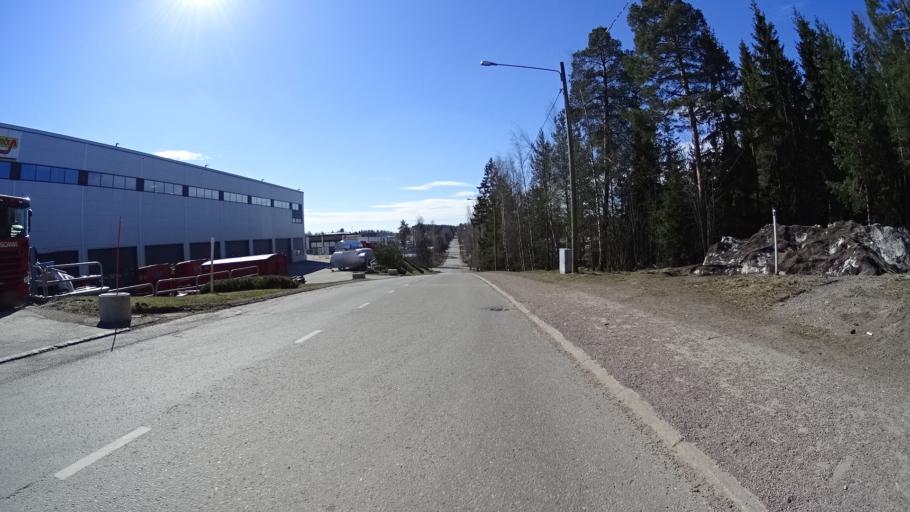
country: FI
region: Uusimaa
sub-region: Helsinki
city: Kilo
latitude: 60.2828
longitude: 24.7589
